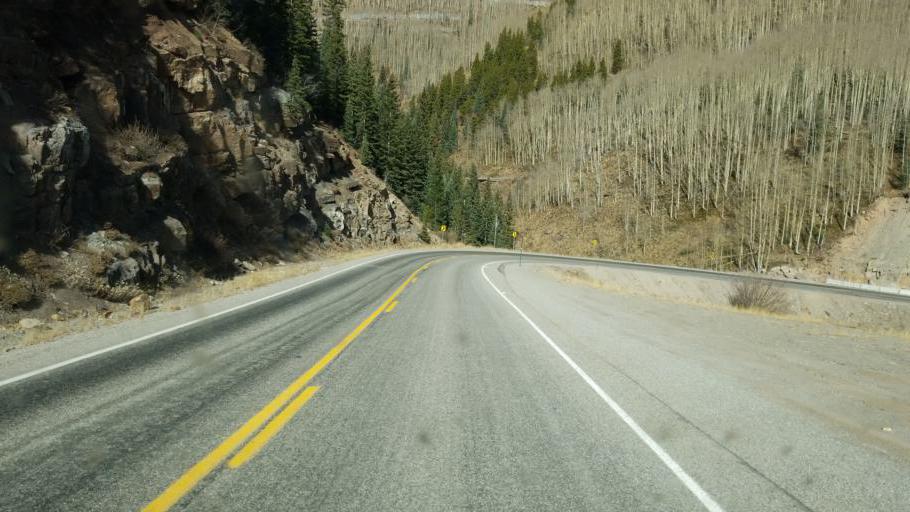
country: US
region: Colorado
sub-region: San Juan County
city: Silverton
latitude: 37.7177
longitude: -107.7560
